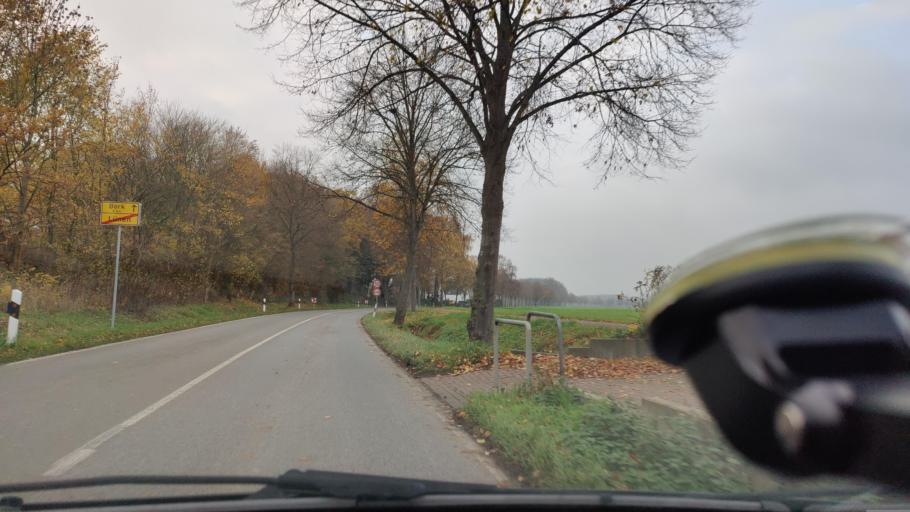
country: DE
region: North Rhine-Westphalia
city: Lunen
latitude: 51.6306
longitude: 7.4826
